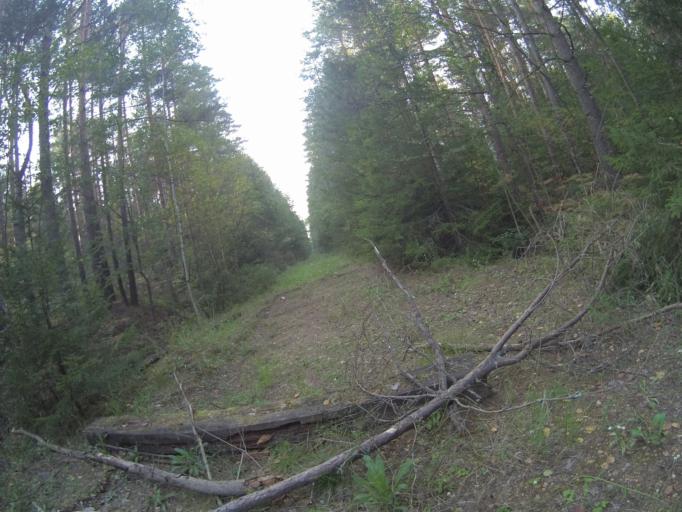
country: RU
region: Vladimir
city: Raduzhnyy
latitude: 55.9861
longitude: 40.2739
